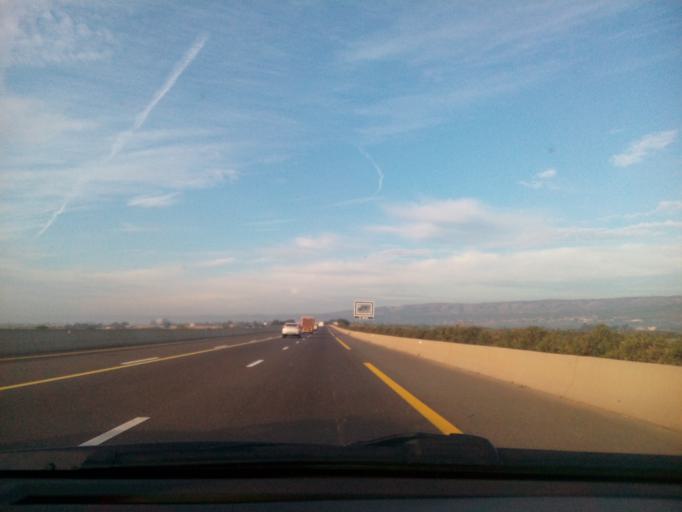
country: DZ
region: Relizane
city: Relizane
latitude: 35.7921
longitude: 0.4490
